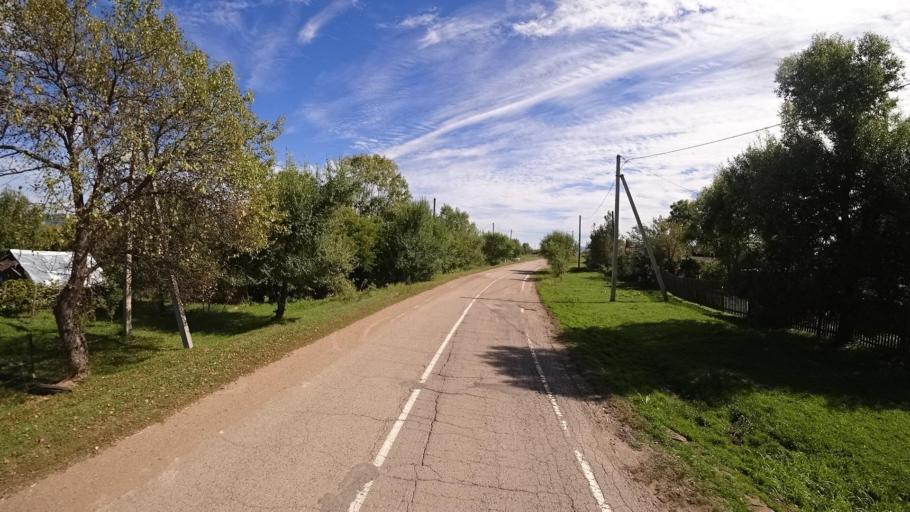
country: RU
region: Primorskiy
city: Yakovlevka
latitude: 44.4273
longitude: 133.5738
